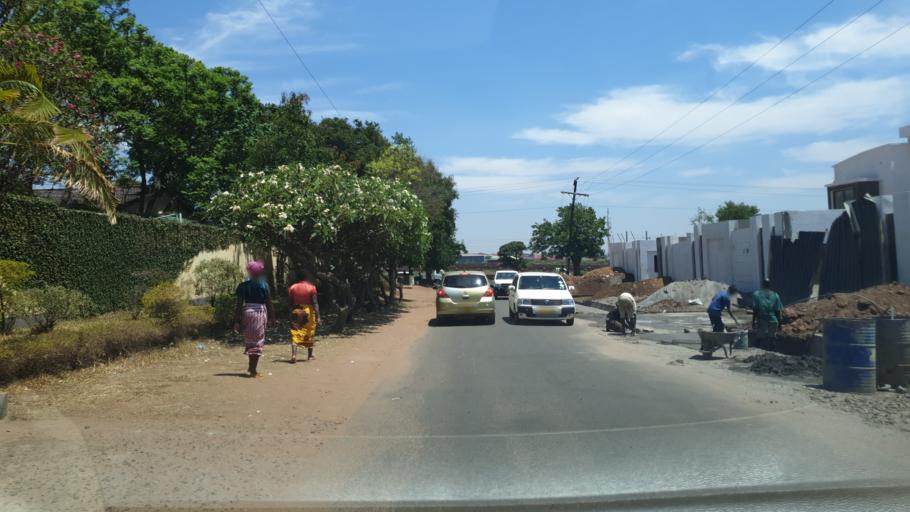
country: MW
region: Central Region
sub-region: Lilongwe District
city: Lilongwe
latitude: -13.9754
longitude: 33.7455
